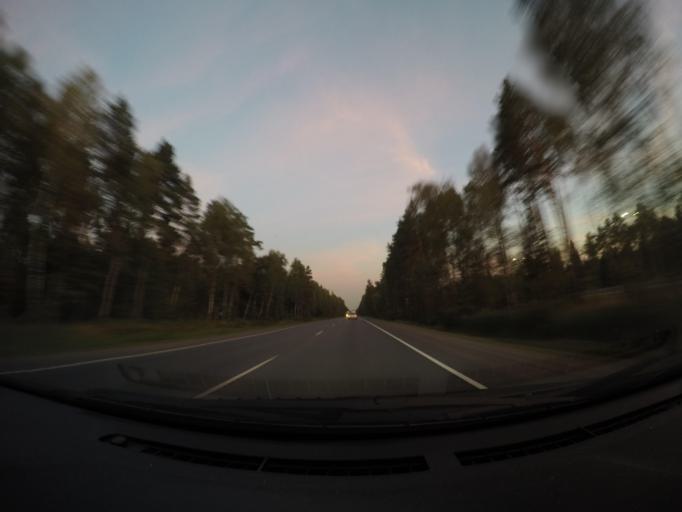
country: RU
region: Moskovskaya
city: Gzhel'
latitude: 55.5660
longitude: 38.3940
